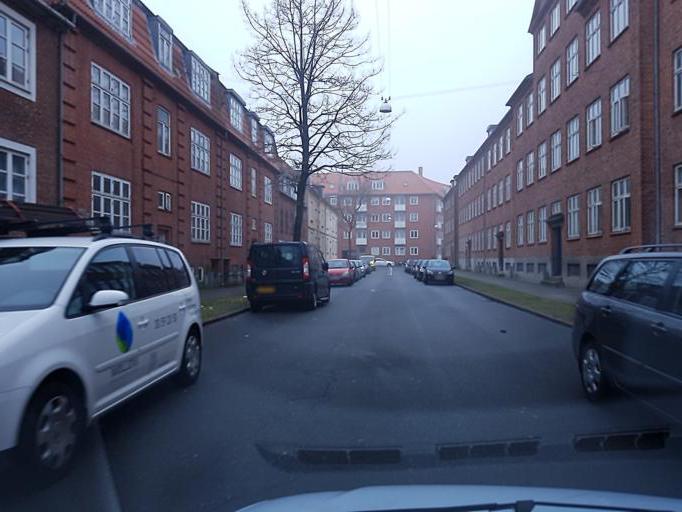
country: DK
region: South Denmark
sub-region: Esbjerg Kommune
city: Esbjerg
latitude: 55.4715
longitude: 8.4401
